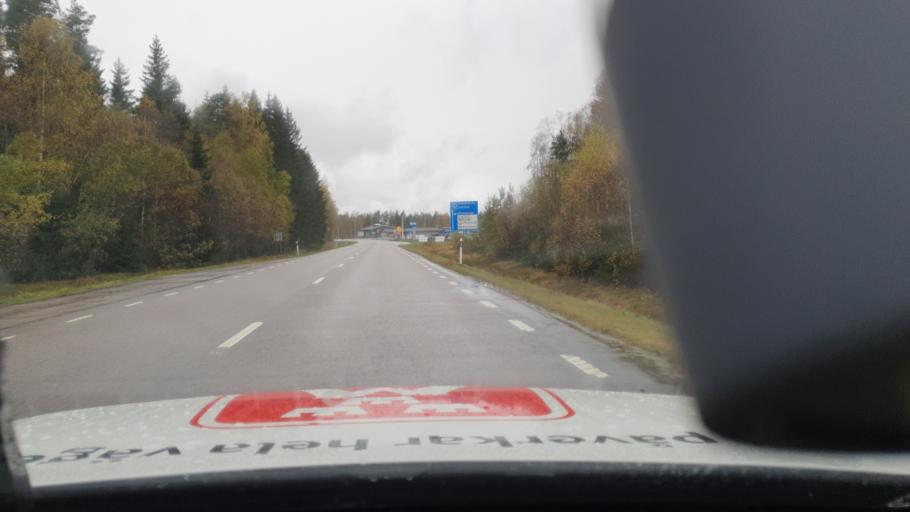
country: SE
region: Vaestra Goetaland
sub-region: Dals-Ed Kommun
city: Ed
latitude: 58.8998
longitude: 11.9514
